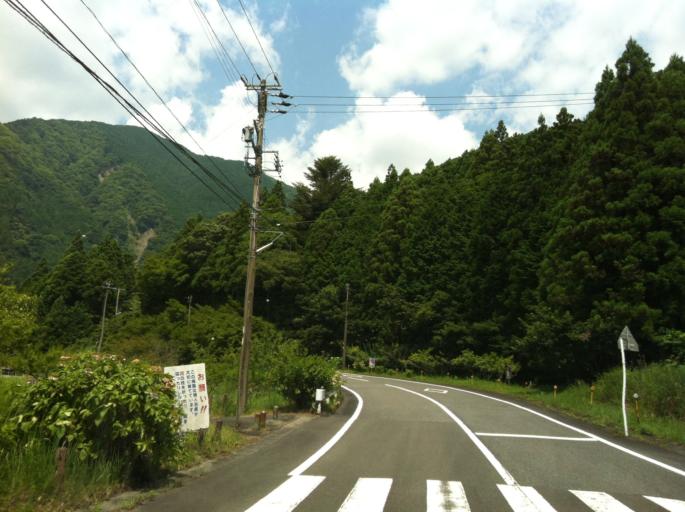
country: JP
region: Shizuoka
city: Fujinomiya
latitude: 35.2667
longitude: 138.3292
